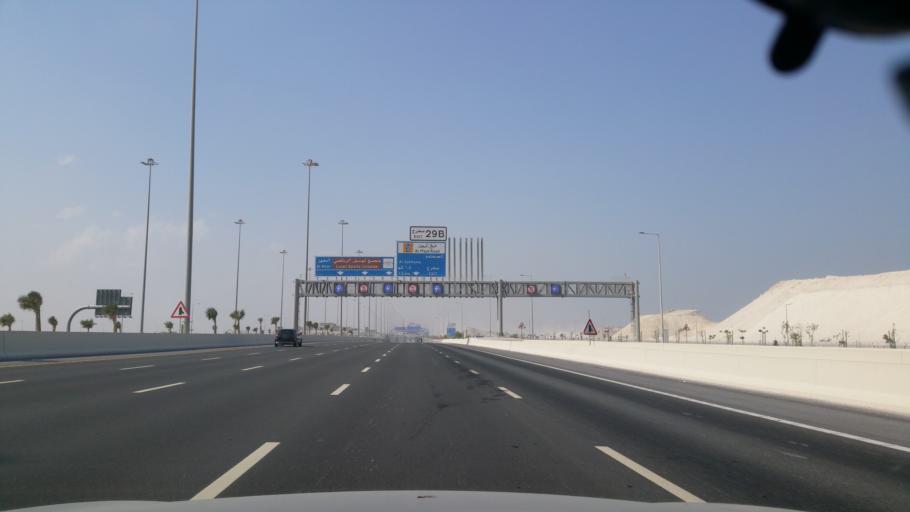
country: QA
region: Baladiyat Umm Salal
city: Umm Salal Muhammad
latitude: 25.4343
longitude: 51.4836
